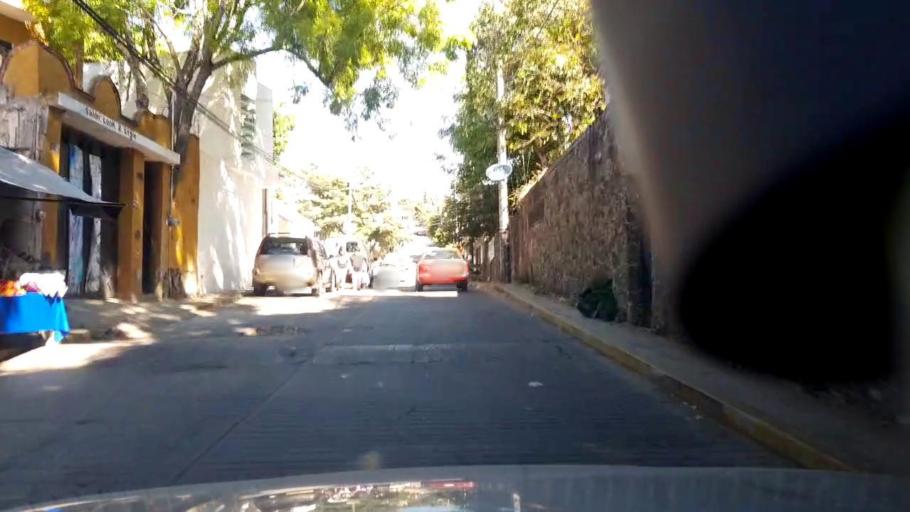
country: MX
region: Morelos
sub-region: Cuernavaca
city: Lomas de Ahuatepec
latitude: 18.9705
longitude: -99.2135
